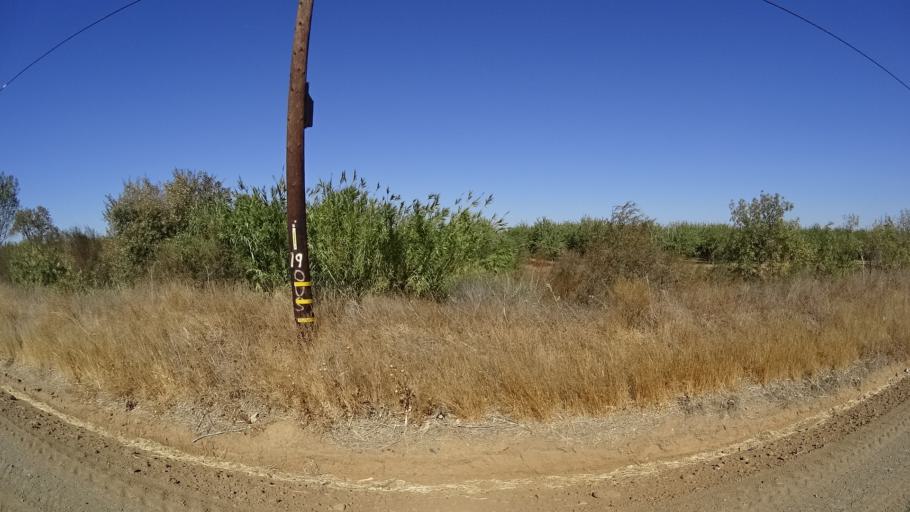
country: US
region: California
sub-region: Yolo County
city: Woodland
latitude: 38.6197
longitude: -121.8424
